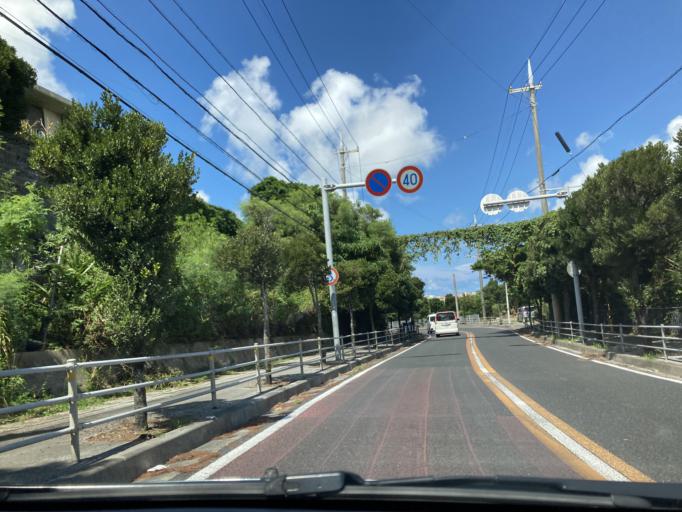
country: JP
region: Okinawa
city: Tomigusuku
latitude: 26.1724
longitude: 127.7214
